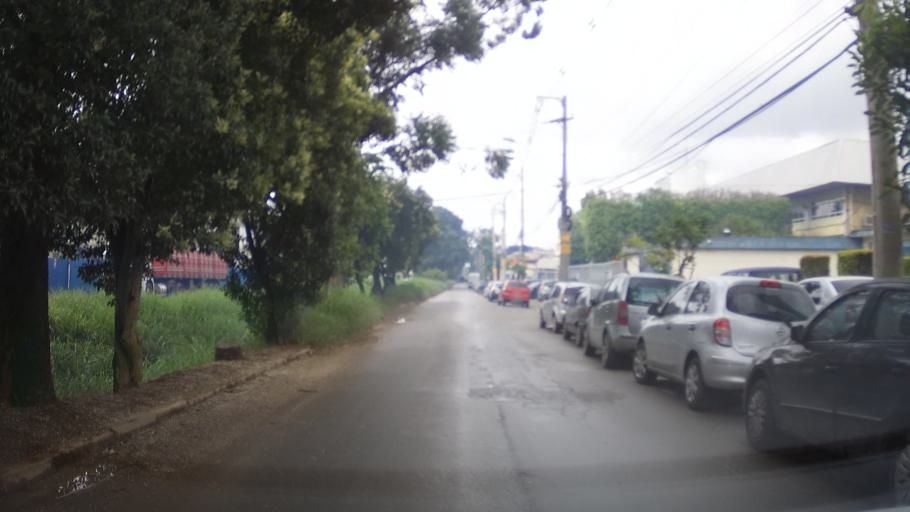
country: BR
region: Sao Paulo
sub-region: Guarulhos
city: Guarulhos
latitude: -23.4673
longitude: -46.4847
